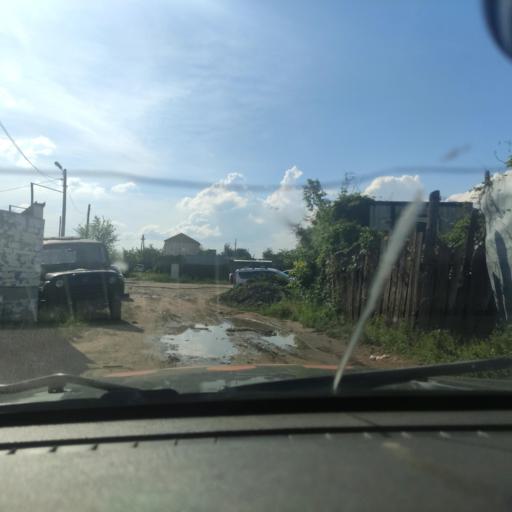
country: RU
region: Samara
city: Zhigulevsk
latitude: 53.4751
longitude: 49.5403
